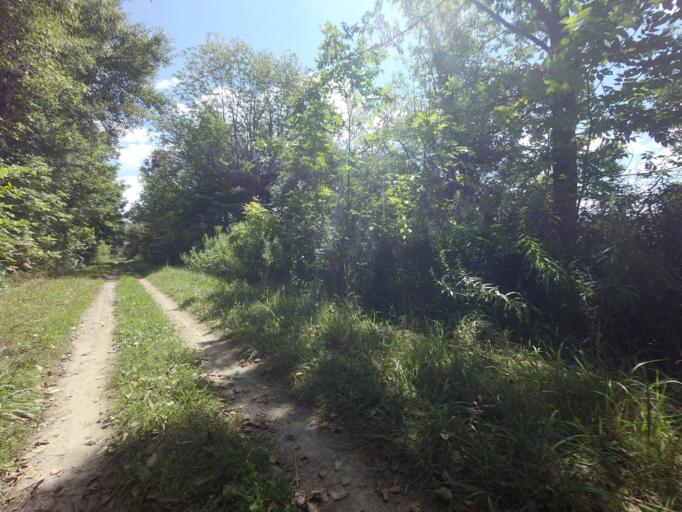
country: CA
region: Ontario
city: Orangeville
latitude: 43.7915
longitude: -80.2649
